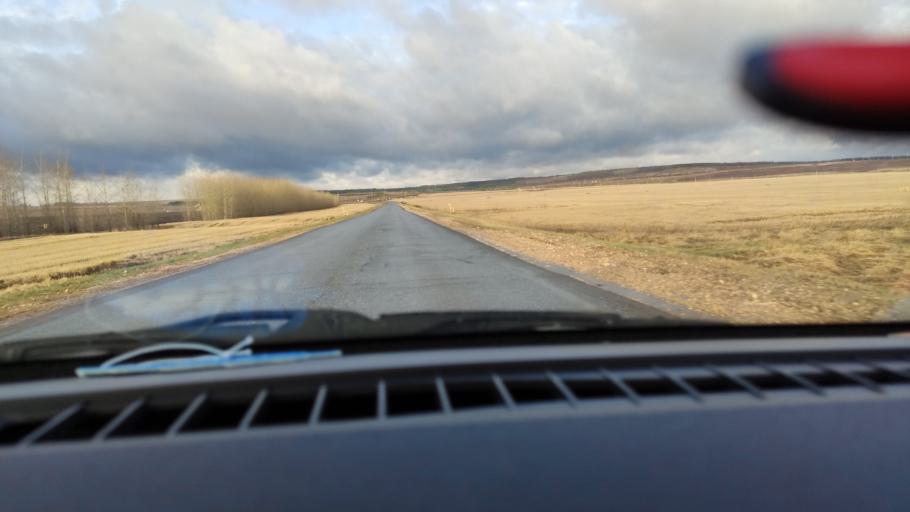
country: RU
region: Tatarstan
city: Russkiy Aktash
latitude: 55.0402
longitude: 52.0509
